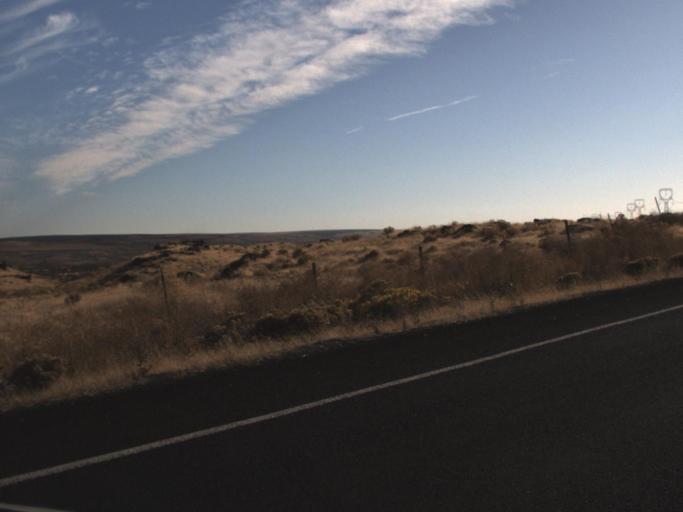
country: US
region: Washington
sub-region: Franklin County
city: Connell
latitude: 46.6401
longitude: -118.8205
